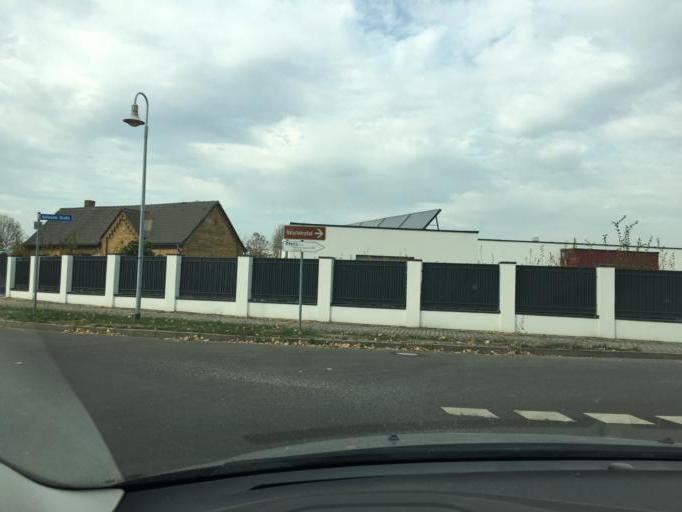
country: DE
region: Saxony
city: Zwochau
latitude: 51.4664
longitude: 12.2695
